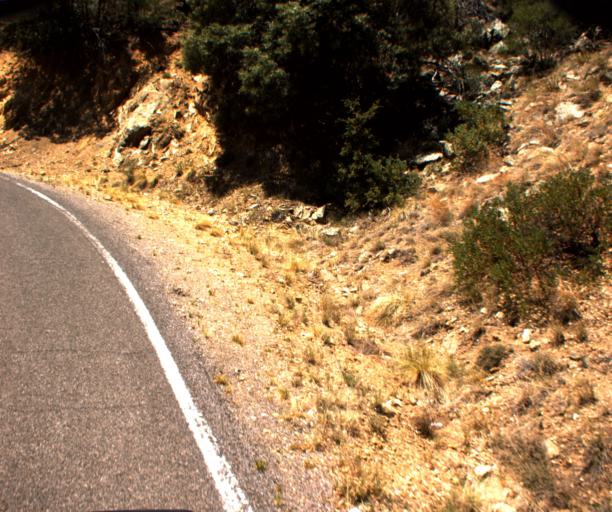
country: US
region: Arizona
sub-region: Graham County
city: Swift Trail Junction
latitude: 32.6647
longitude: -109.8016
